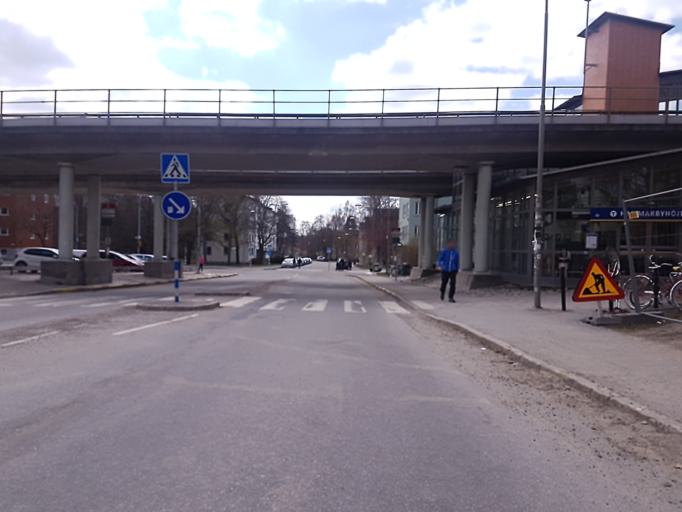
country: SE
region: Stockholm
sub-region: Stockholms Kommun
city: OEstermalm
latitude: 59.2951
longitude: 18.1067
